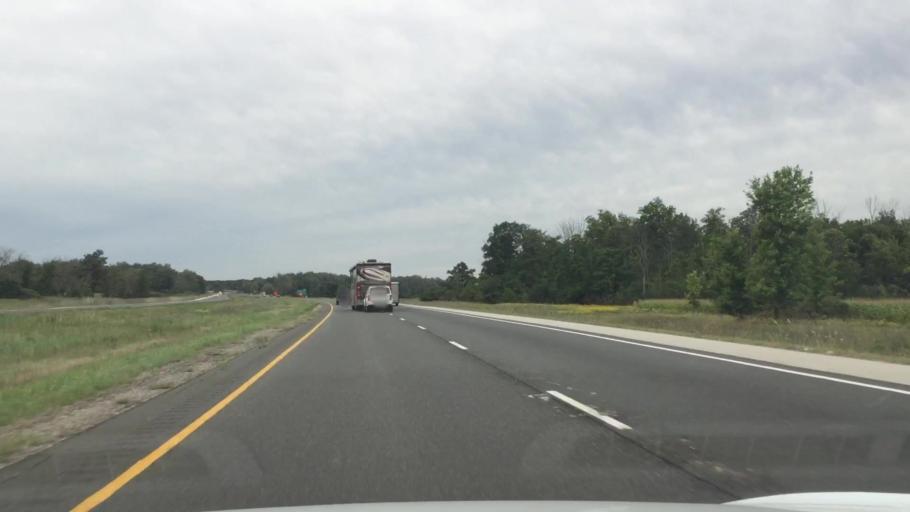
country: CA
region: Ontario
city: London
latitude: 42.9049
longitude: -81.2477
